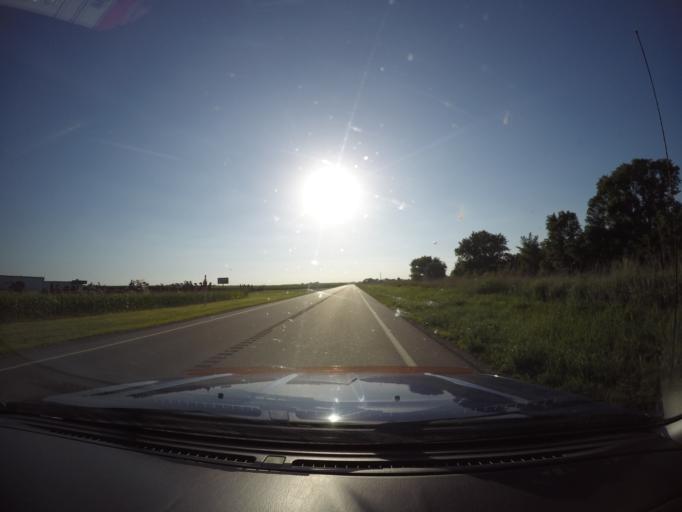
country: US
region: Kansas
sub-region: Shawnee County
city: Rossville
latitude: 39.1188
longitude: -95.9136
